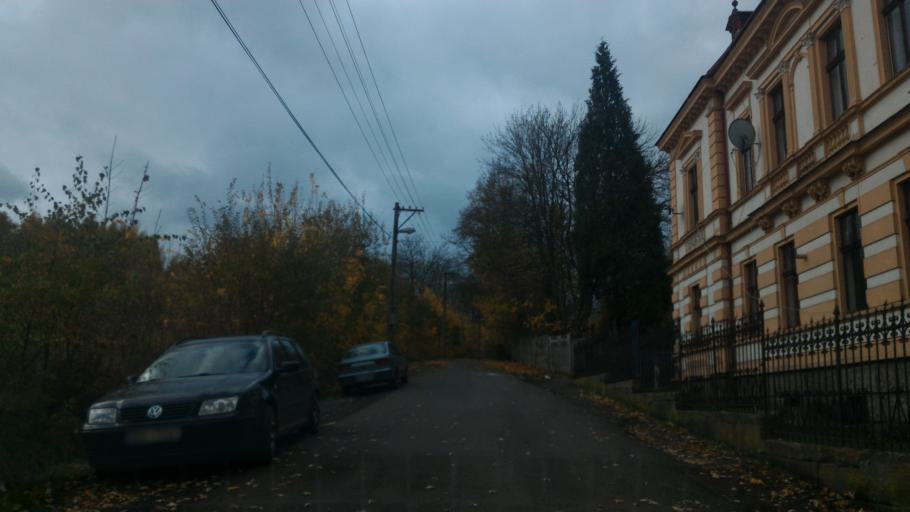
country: CZ
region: Ustecky
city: Varnsdorf
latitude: 50.9027
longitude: 14.6329
